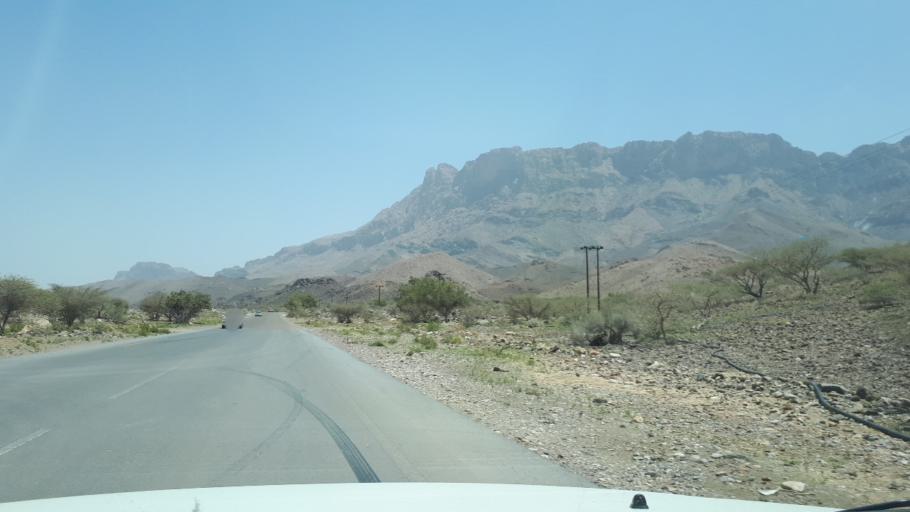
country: OM
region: Muhafazat ad Dakhiliyah
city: Bahla'
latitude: 23.1671
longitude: 57.1587
